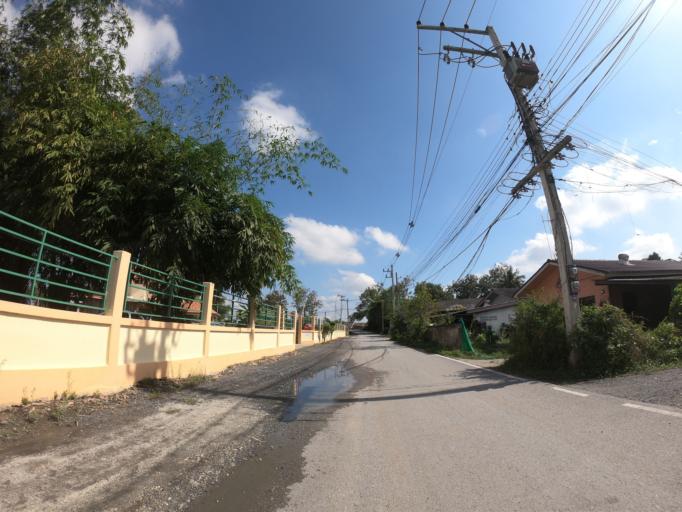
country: TH
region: Chiang Mai
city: San Sai
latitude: 18.8453
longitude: 99.0533
